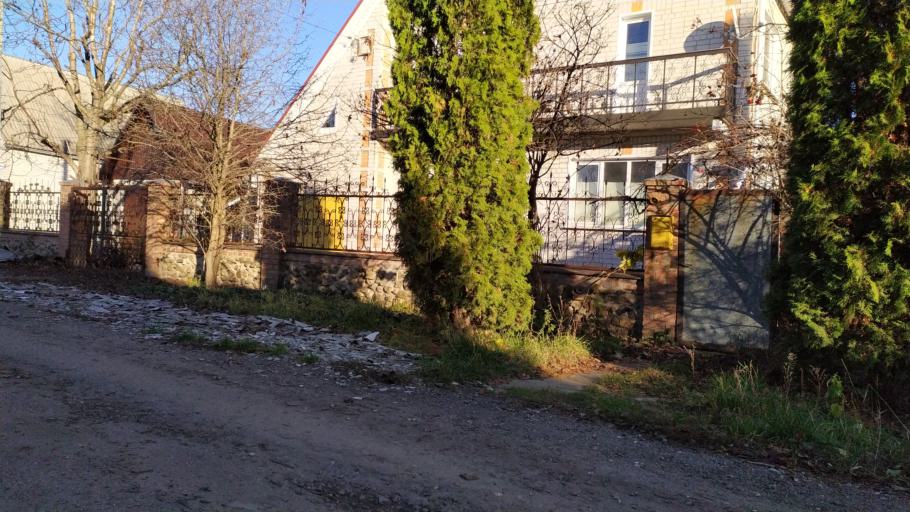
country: RU
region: Kursk
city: Kursk
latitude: 51.6458
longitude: 36.1379
